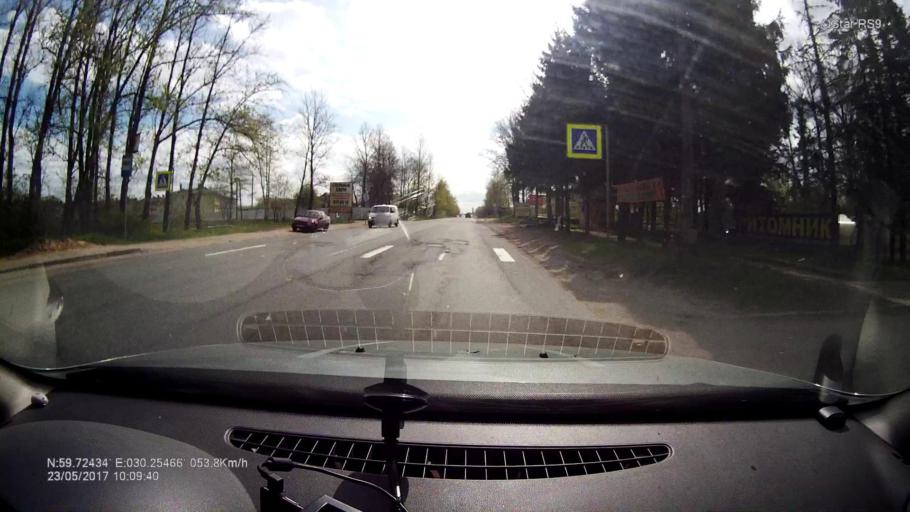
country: RU
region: St.-Petersburg
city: Aleksandrovskaya
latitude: 59.7243
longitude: 30.2547
